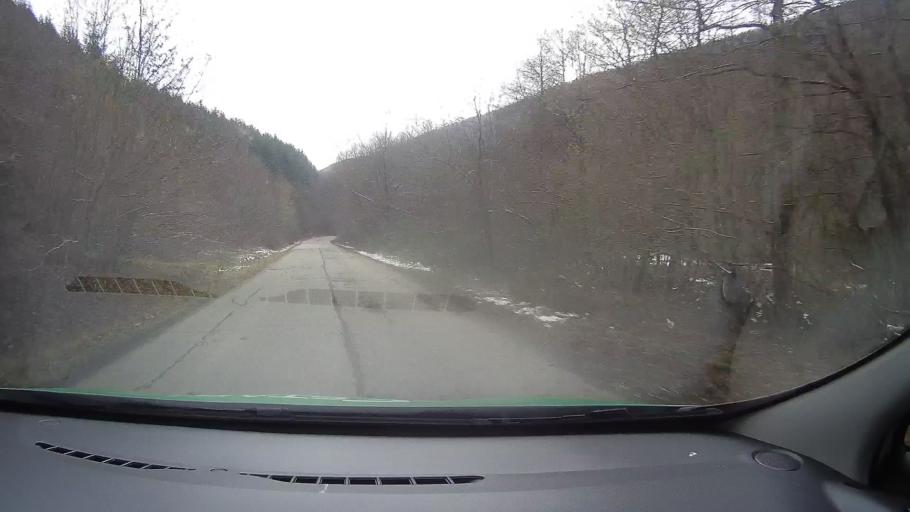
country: RO
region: Hunedoara
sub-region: Comuna Balsa
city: Balsa
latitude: 46.0011
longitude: 23.1501
